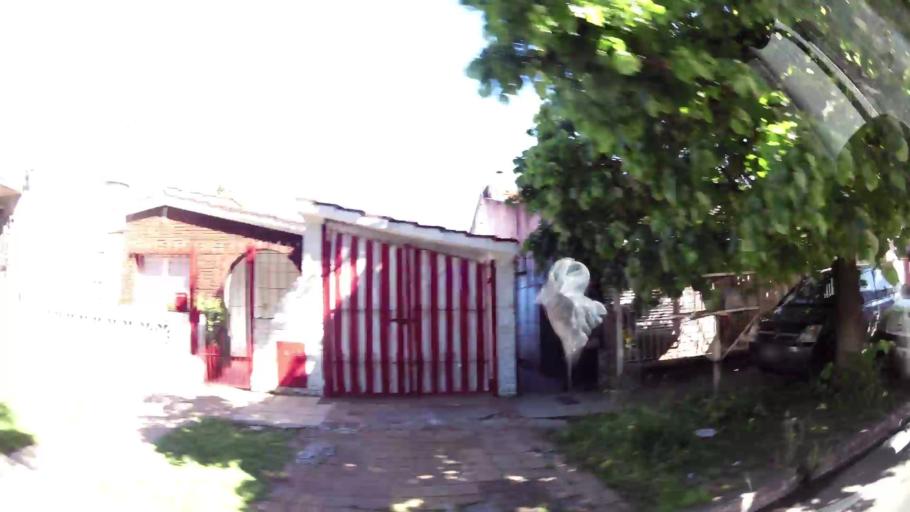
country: AR
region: Buenos Aires
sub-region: Partido de Quilmes
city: Quilmes
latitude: -34.7023
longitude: -58.3018
